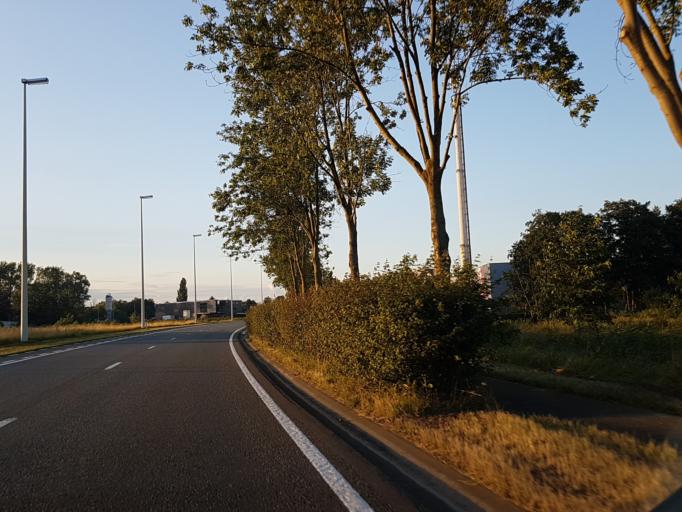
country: BE
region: Flanders
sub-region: Provincie Oost-Vlaanderen
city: Hamme
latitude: 51.0696
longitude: 4.1243
